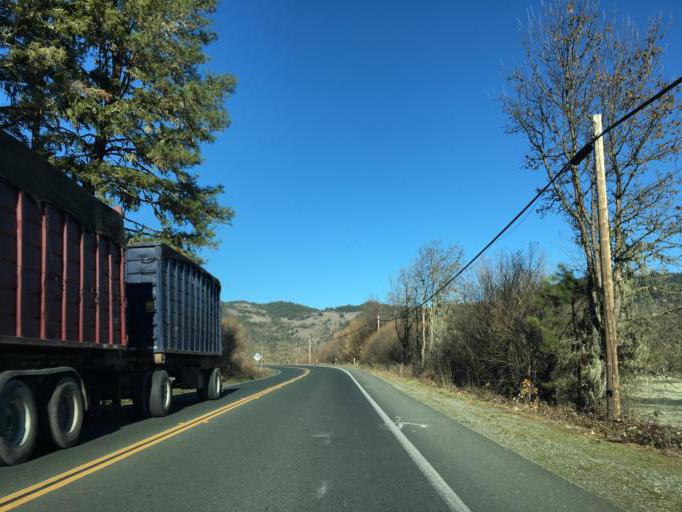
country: US
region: California
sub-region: Mendocino County
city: Brooktrails
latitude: 39.4484
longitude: -123.3492
